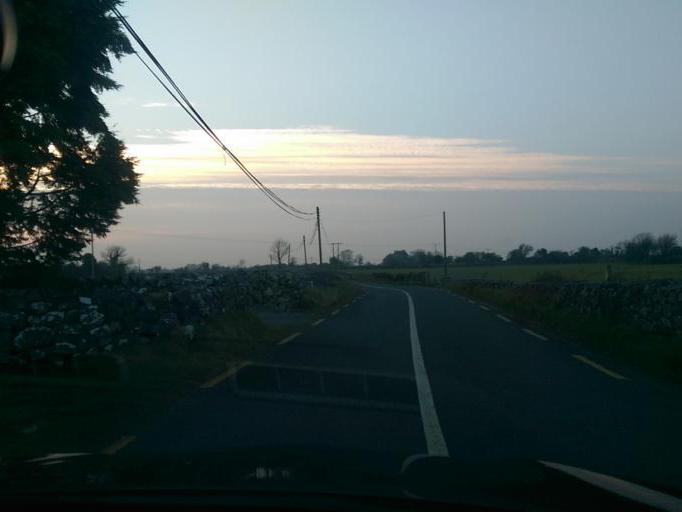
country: IE
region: Connaught
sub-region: County Galway
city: Loughrea
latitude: 53.2146
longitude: -8.6098
